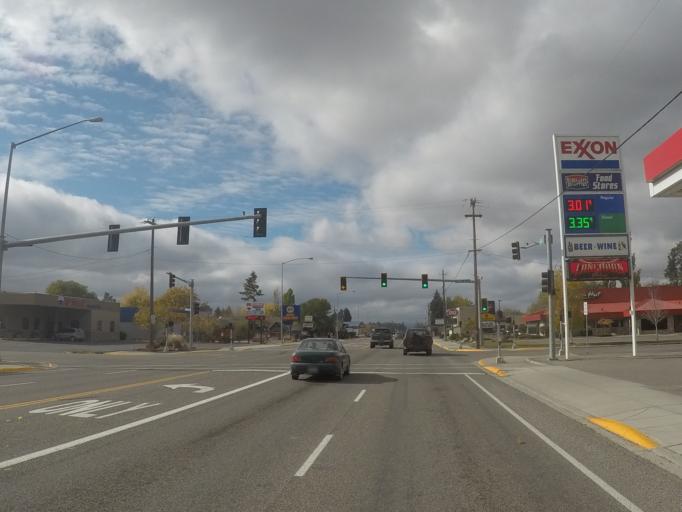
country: US
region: Montana
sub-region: Flathead County
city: Columbia Falls
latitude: 48.3707
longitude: -114.1888
